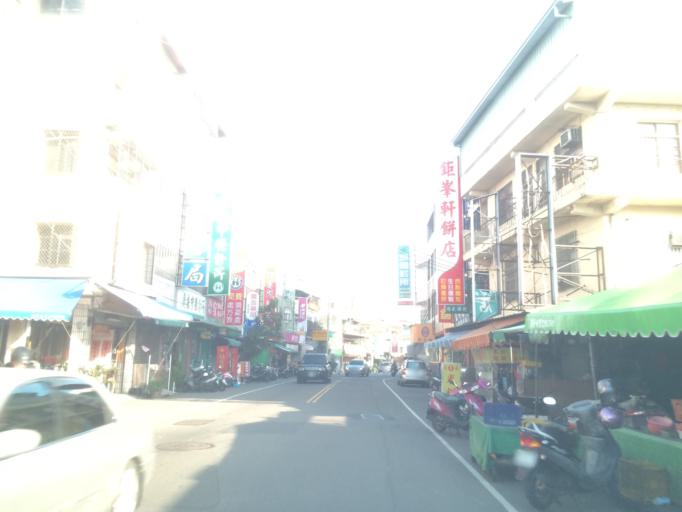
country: TW
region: Taiwan
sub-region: Taichung City
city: Taichung
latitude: 24.1920
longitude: 120.6825
